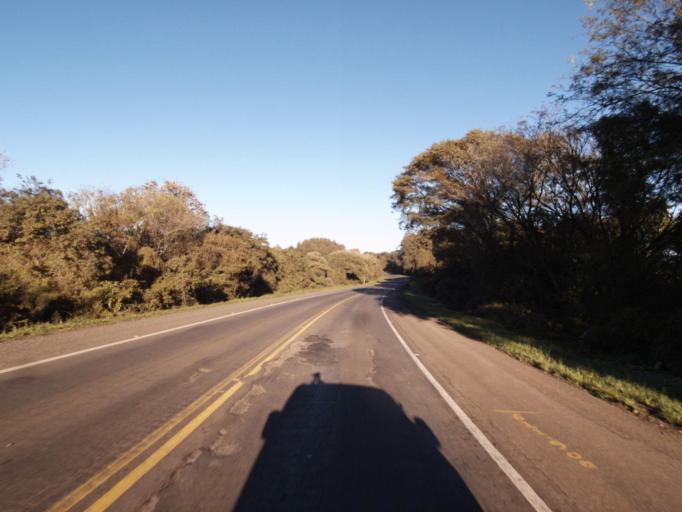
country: BR
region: Santa Catarina
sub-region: Sao Lourenco Do Oeste
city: Sao Lourenco dOeste
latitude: -26.7746
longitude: -53.2723
